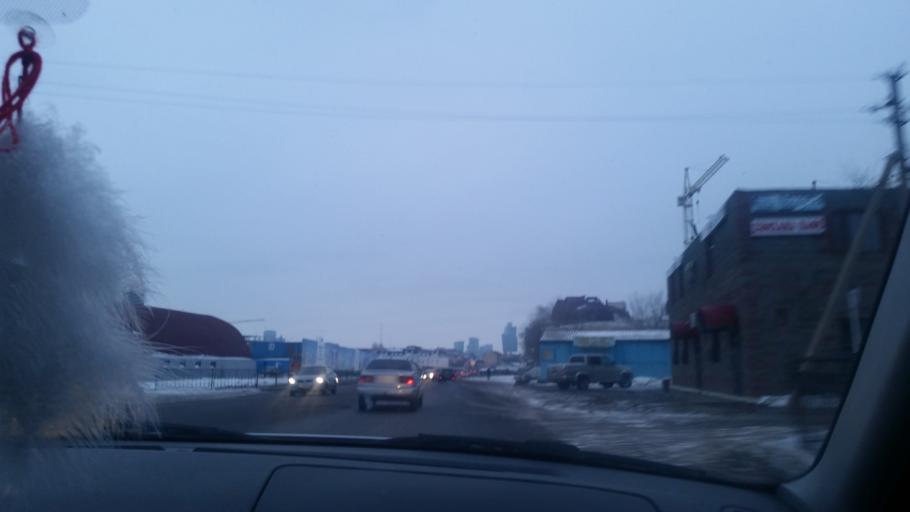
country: KZ
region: Astana Qalasy
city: Astana
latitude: 51.1450
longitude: 71.4596
